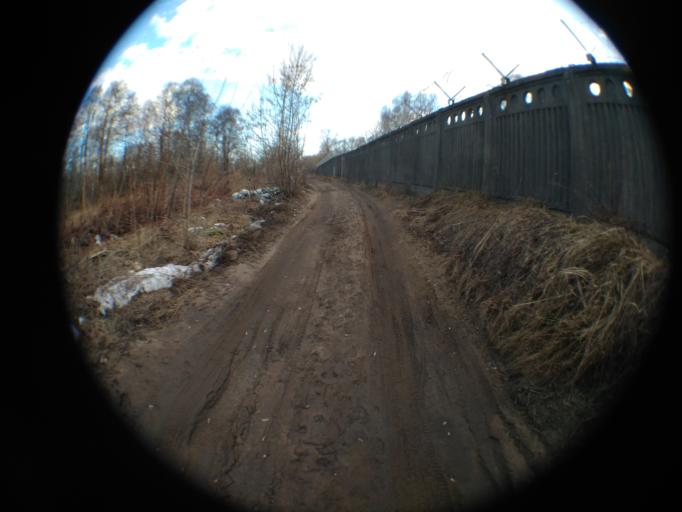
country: RU
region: Moskovskaya
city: Kratovo
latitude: 55.5703
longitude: 38.1699
